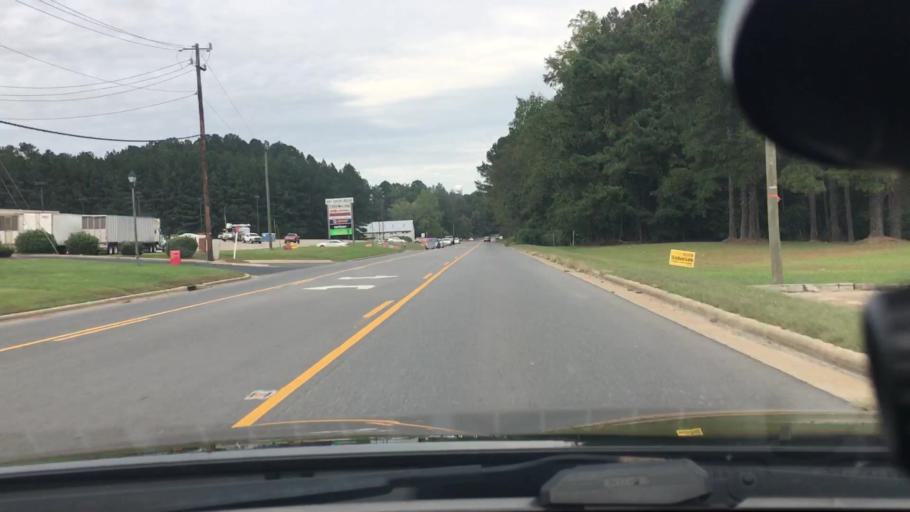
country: US
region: North Carolina
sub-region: Montgomery County
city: Troy
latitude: 35.3457
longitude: -79.9137
